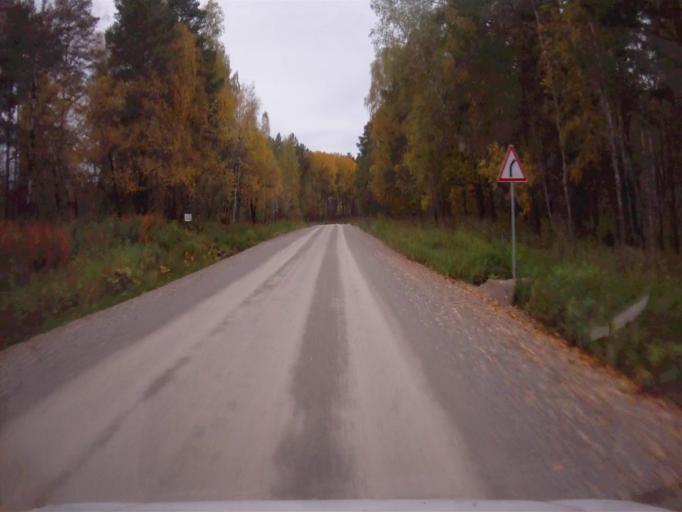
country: RU
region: Chelyabinsk
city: Nyazepetrovsk
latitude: 56.0671
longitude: 59.4368
